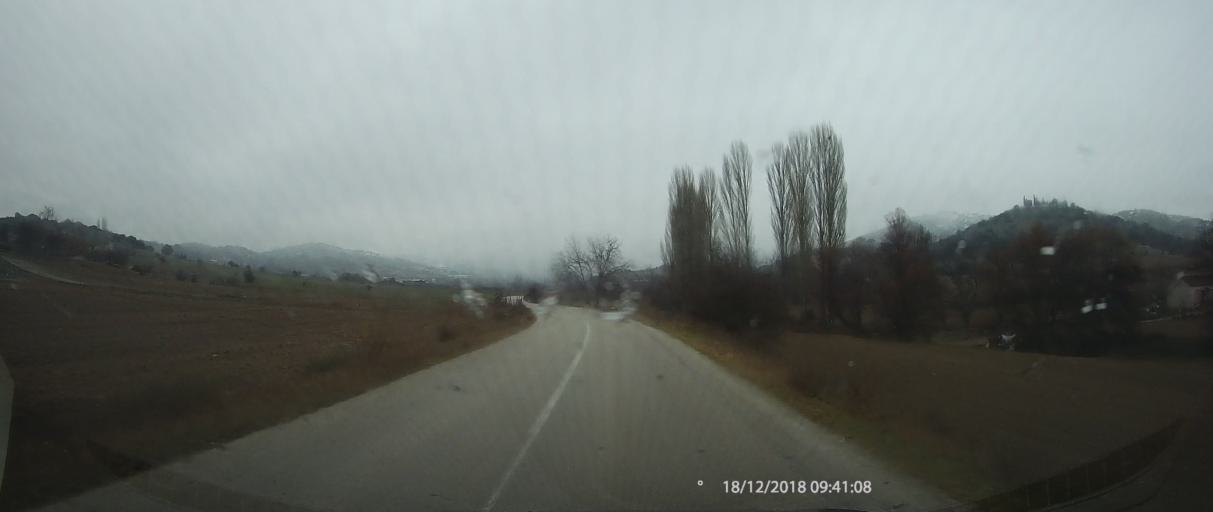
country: GR
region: Thessaly
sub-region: Nomos Larisis
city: Elassona
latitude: 40.0087
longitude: 22.2309
